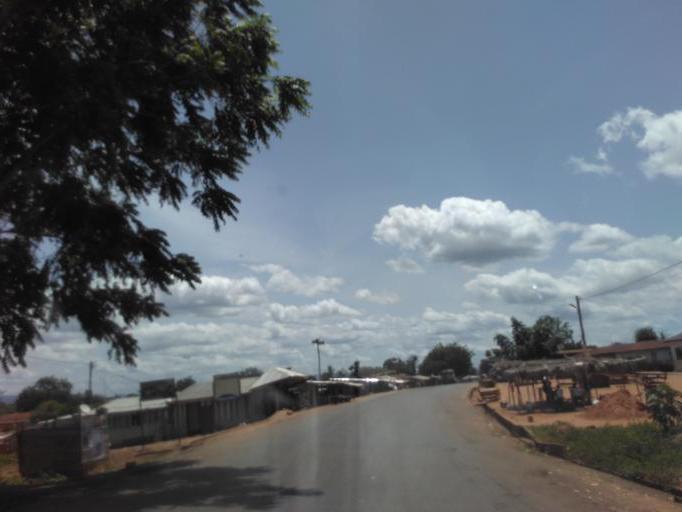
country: GH
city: Akropong
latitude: 6.0638
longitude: -0.0986
